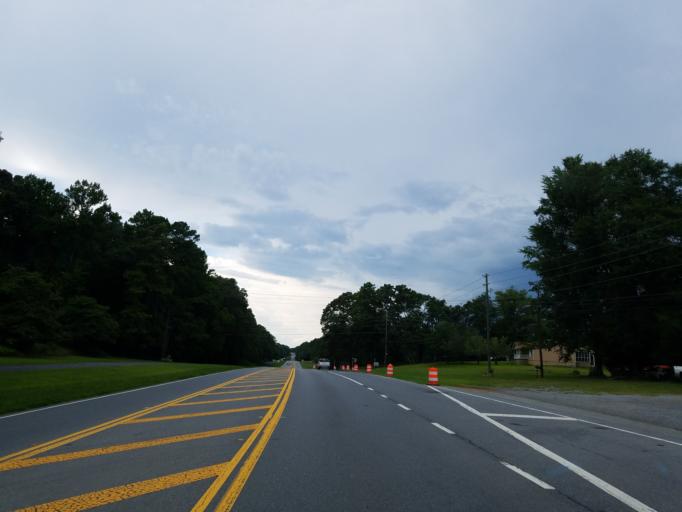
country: US
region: Georgia
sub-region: Bartow County
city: Adairsville
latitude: 34.2846
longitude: -84.8701
